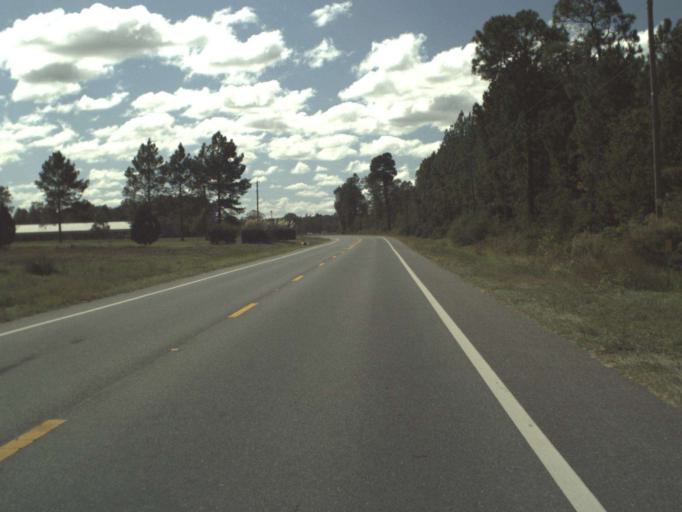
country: US
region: Florida
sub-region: Washington County
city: Chipley
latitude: 30.7355
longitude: -85.6079
